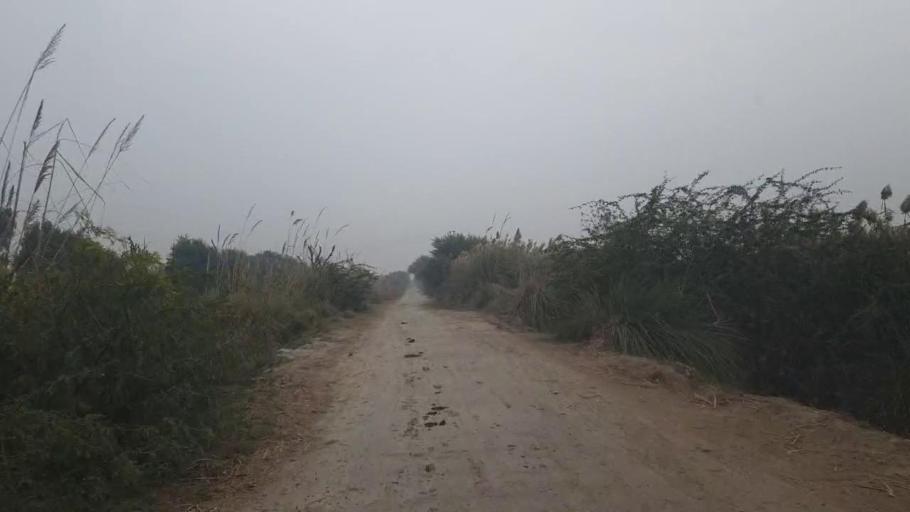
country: PK
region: Sindh
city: Tando Adam
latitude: 25.7484
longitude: 68.7042
